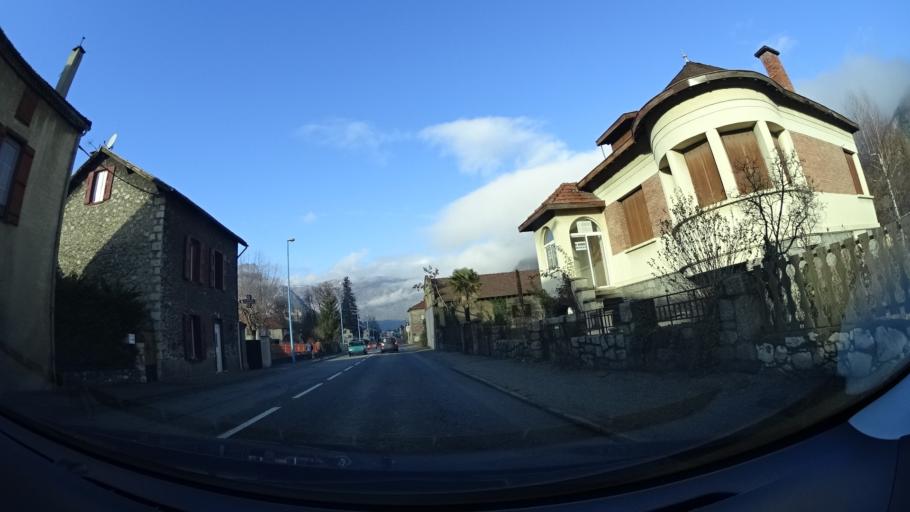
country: FR
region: Midi-Pyrenees
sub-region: Departement de l'Ariege
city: Tarascon-sur-Ariege
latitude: 42.8411
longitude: 1.6025
